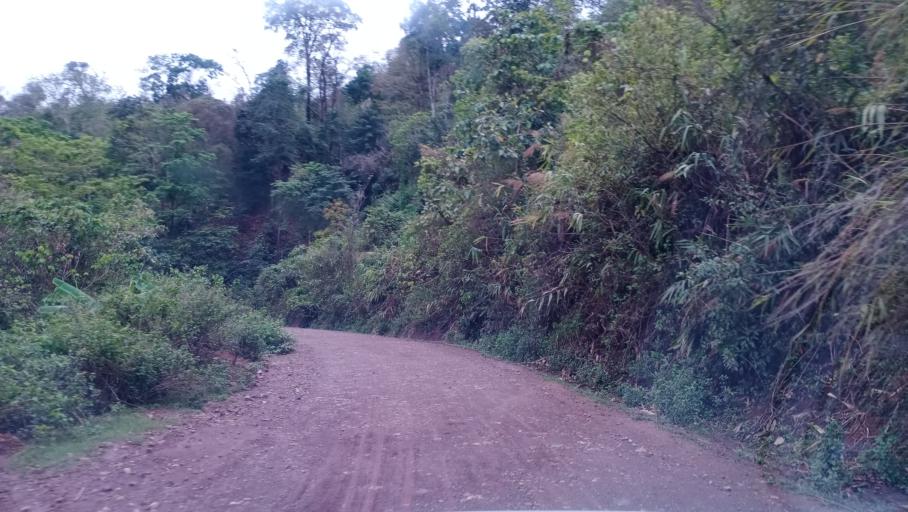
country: LA
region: Phongsali
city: Phongsali
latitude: 21.3405
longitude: 102.0765
